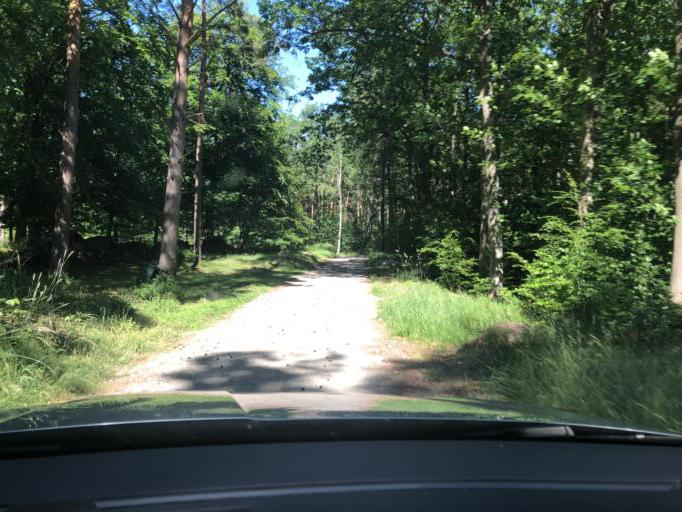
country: SE
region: Blekinge
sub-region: Solvesborgs Kommun
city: Soelvesborg
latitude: 56.1338
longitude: 14.6145
